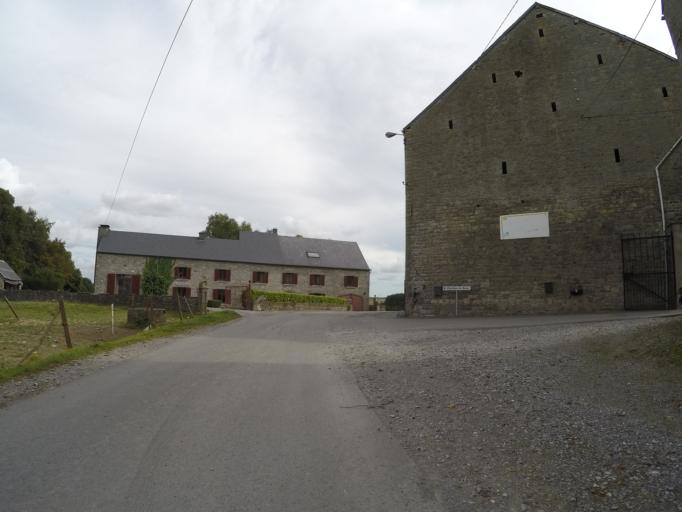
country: BE
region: Wallonia
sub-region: Province de Namur
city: Assesse
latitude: 50.3144
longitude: 4.9781
